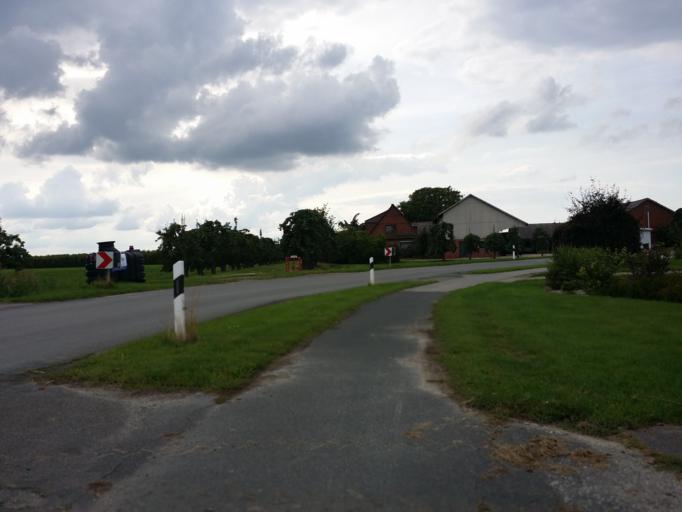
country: DE
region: Lower Saxony
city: Oederquart
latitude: 53.7846
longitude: 9.2292
